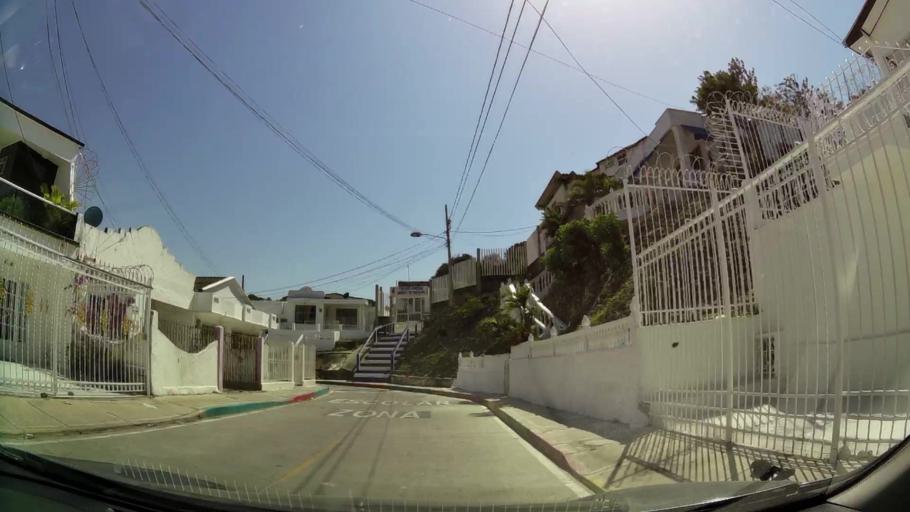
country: CO
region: Bolivar
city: Cartagena
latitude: 10.4366
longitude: -75.5216
